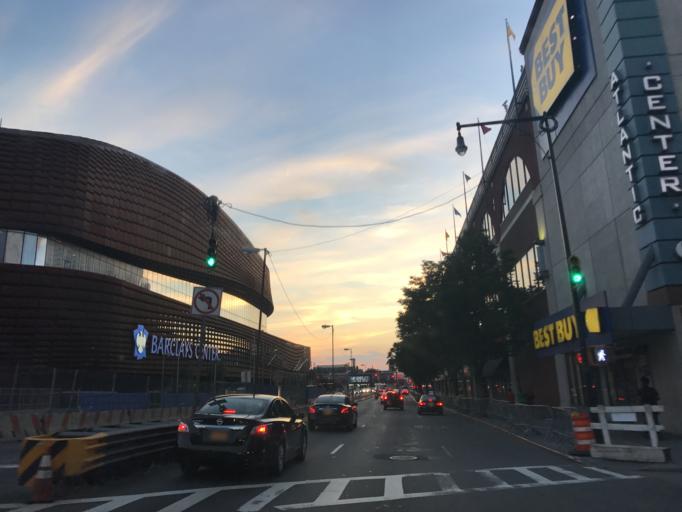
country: US
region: New York
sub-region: Kings County
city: Brooklyn
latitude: 40.6831
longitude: -73.9737
